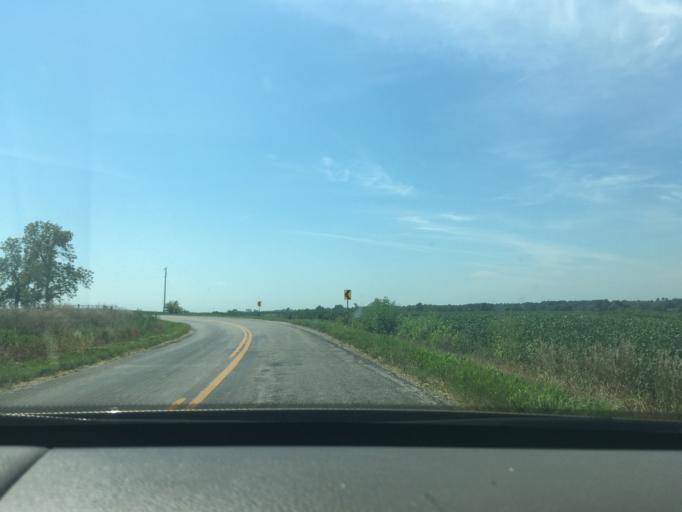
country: US
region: Missouri
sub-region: Nodaway County
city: Maryville
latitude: 40.1998
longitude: -94.7400
